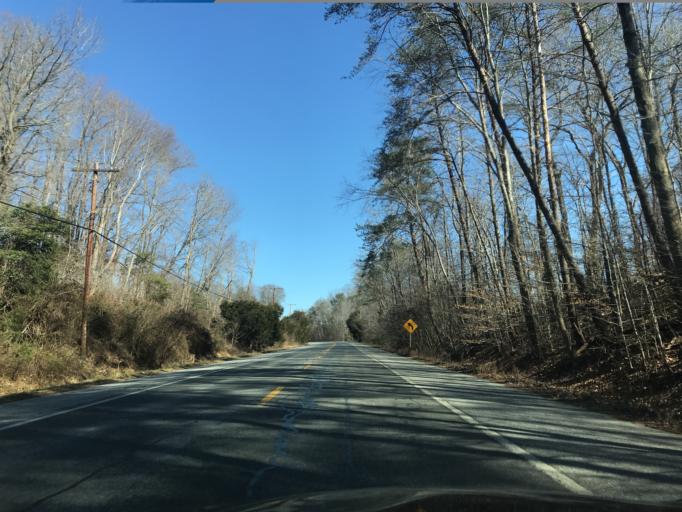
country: US
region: Maryland
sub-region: Charles County
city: Indian Head
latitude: 38.5424
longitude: -77.1830
